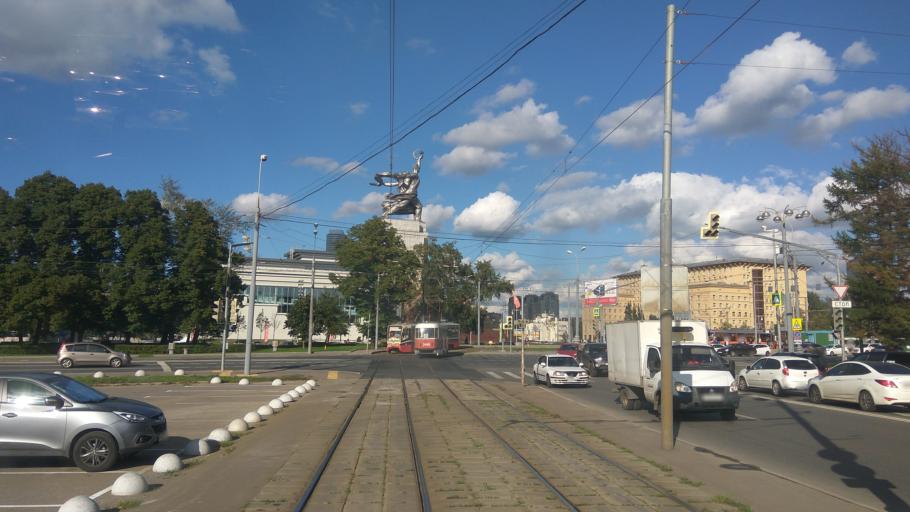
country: RU
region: Moscow
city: Rostokino
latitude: 55.8270
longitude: 37.6445
